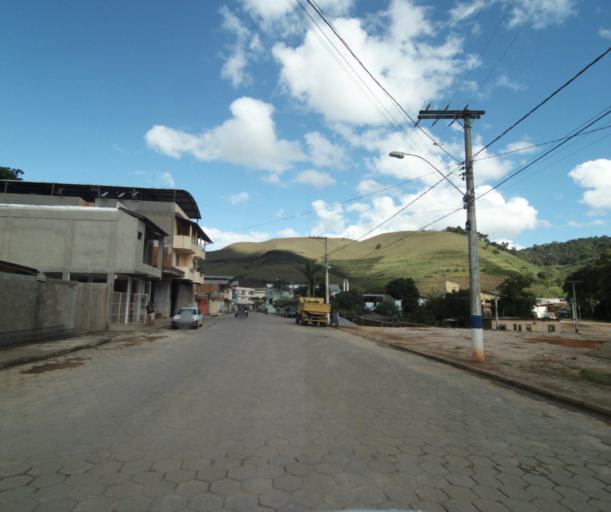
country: BR
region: Espirito Santo
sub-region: Irupi
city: Irupi
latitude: -20.5368
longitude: -41.6661
